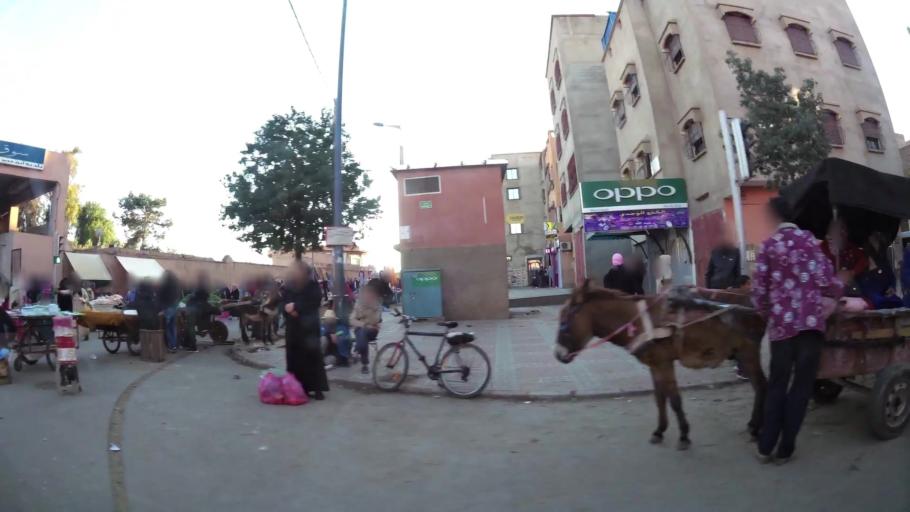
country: MA
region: Marrakech-Tensift-Al Haouz
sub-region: Kelaa-Des-Sraghna
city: Sidi Abdallah
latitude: 32.2415
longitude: -7.9538
